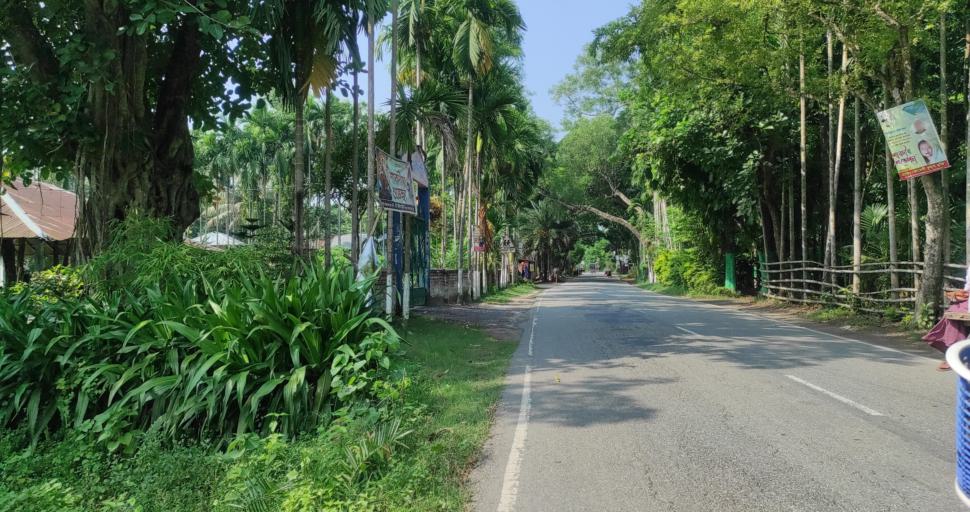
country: BD
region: Rajshahi
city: Ishurdi
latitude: 24.2835
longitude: 89.0650
